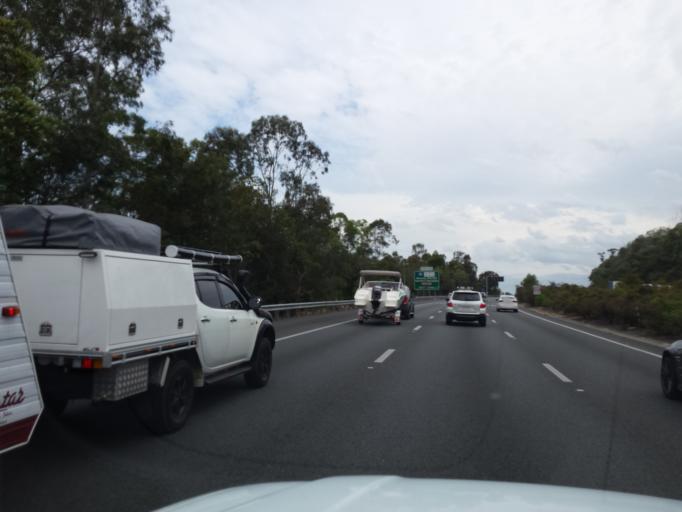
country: AU
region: Queensland
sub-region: Gold Coast
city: Nerang
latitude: -27.9664
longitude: 153.3466
